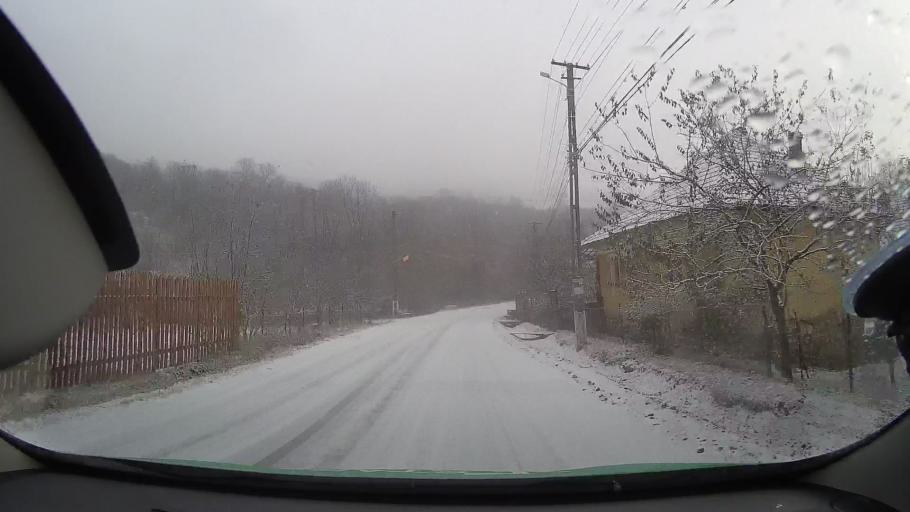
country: RO
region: Alba
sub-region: Comuna Livezile
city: Livezile
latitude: 46.3659
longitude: 23.6063
